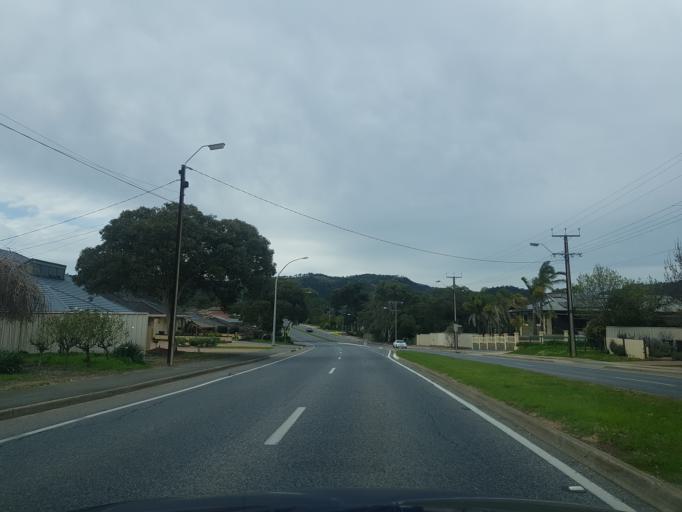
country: AU
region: South Australia
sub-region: Campbelltown
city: Athelstone
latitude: -34.8526
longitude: 138.7066
